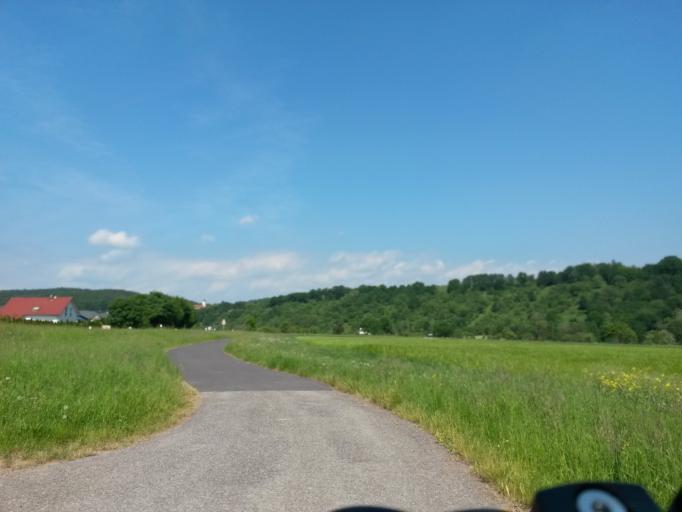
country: DE
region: Bavaria
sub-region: Regierungsbezirk Unterfranken
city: Euerdorf
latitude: 50.1611
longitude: 10.0178
